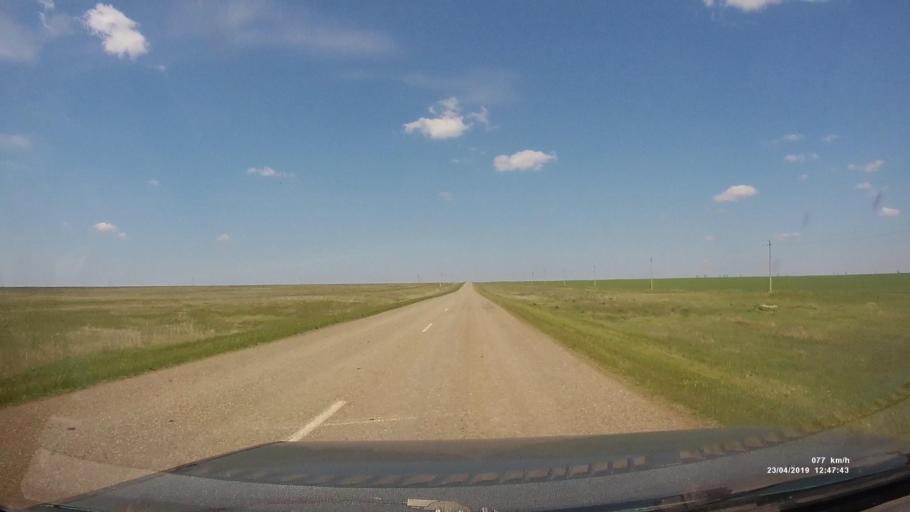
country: RU
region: Kalmykiya
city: Yashalta
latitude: 46.5153
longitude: 42.6387
